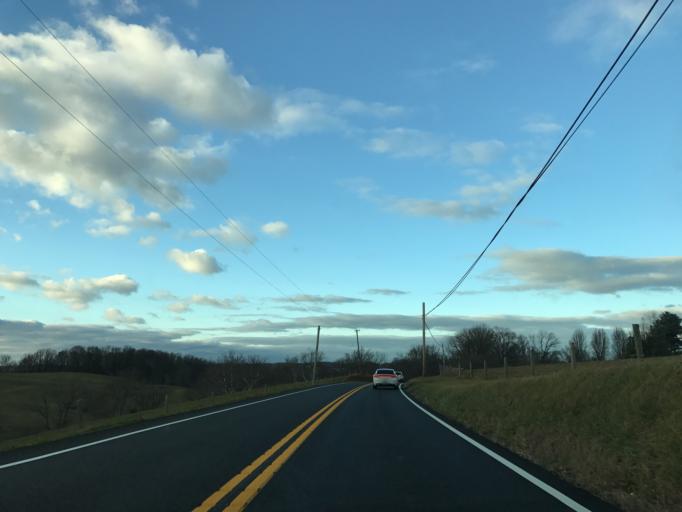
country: US
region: Maryland
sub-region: Harford County
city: Aberdeen
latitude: 39.6081
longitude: -76.1986
